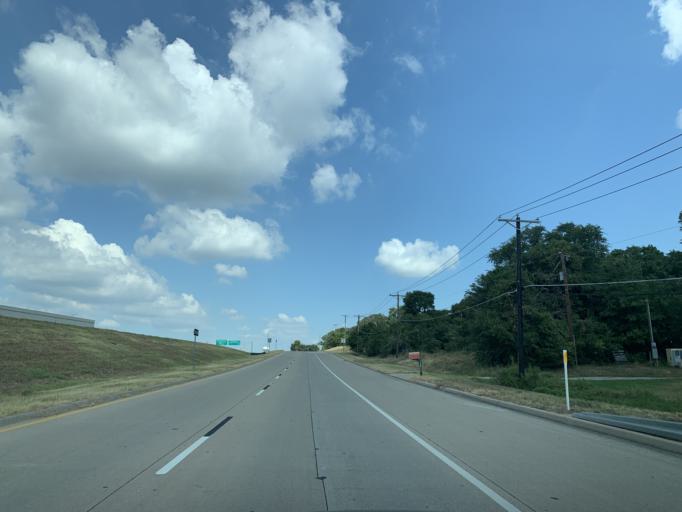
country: US
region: Texas
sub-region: Tarrant County
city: Lakeside
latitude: 32.8502
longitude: -97.5042
